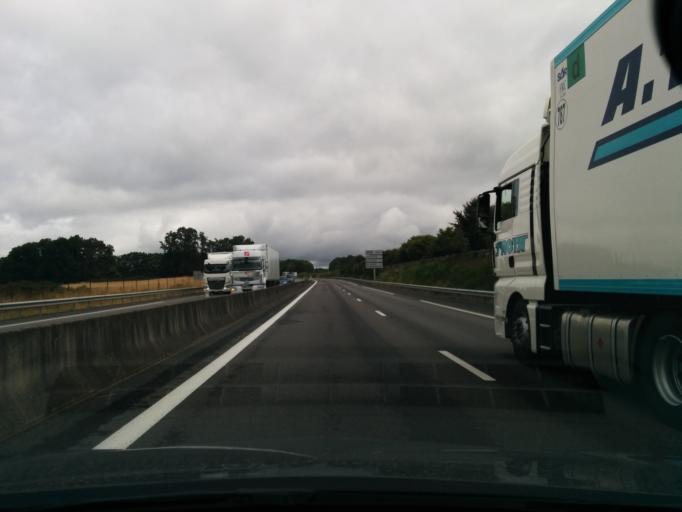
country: FR
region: Limousin
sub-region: Departement de la Correze
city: Uzerche
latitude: 45.3814
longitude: 1.5747
